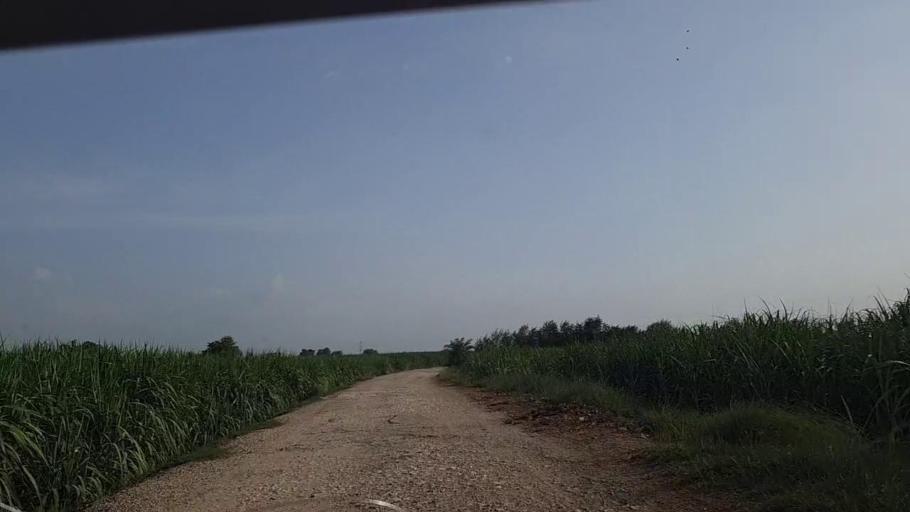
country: PK
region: Sindh
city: Ghotki
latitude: 27.9908
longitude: 69.2622
